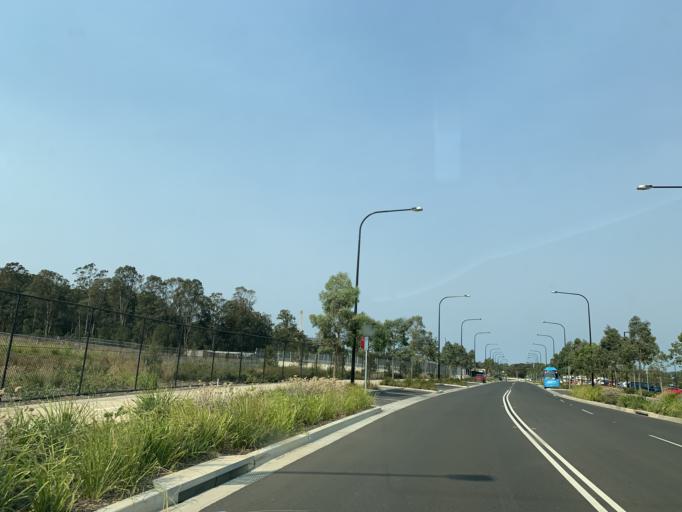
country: AU
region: New South Wales
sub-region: Blacktown
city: Rouse Hill
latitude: -33.6930
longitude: 150.9028
